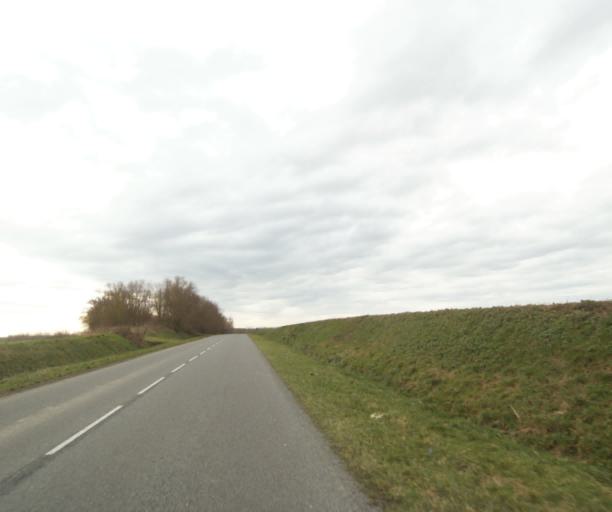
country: FR
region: Nord-Pas-de-Calais
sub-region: Departement du Nord
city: Sebourg
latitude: 50.3289
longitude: 3.6339
